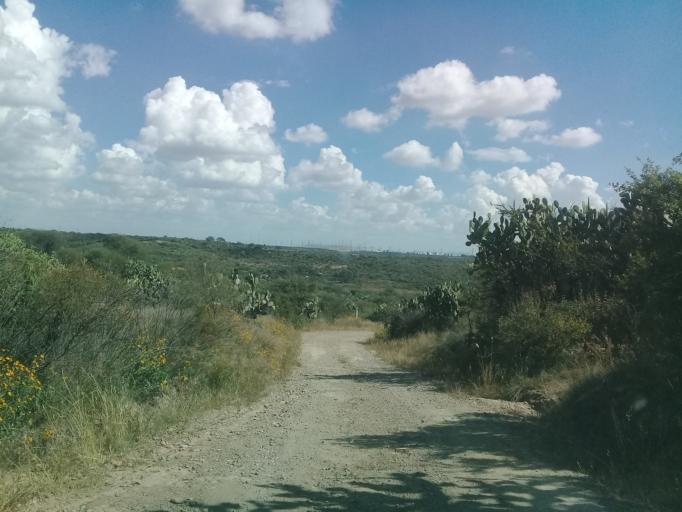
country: MX
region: Aguascalientes
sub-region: Aguascalientes
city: San Sebastian [Fraccionamiento]
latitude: 21.7781
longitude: -102.2497
